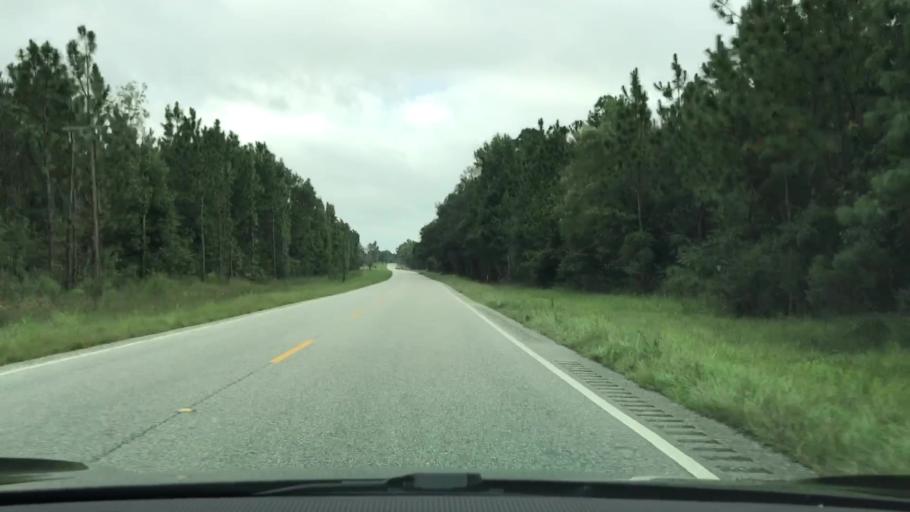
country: US
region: Alabama
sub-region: Geneva County
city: Samson
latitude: 31.0507
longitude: -86.1010
